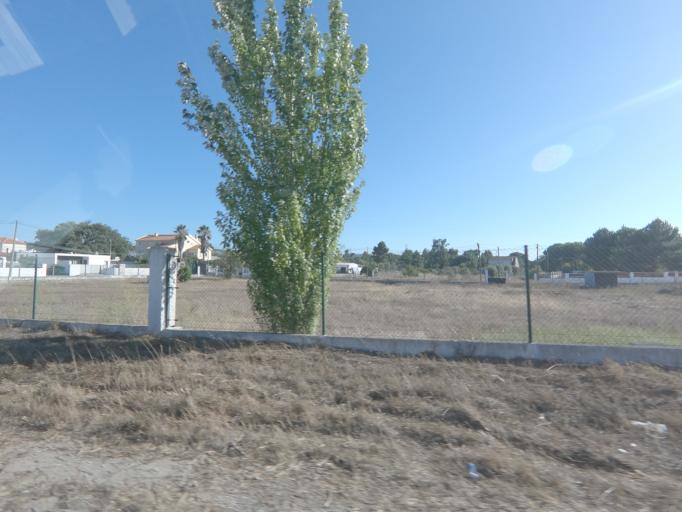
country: PT
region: Setubal
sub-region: Palmela
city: Quinta do Anjo
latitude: 38.5943
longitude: -8.9269
